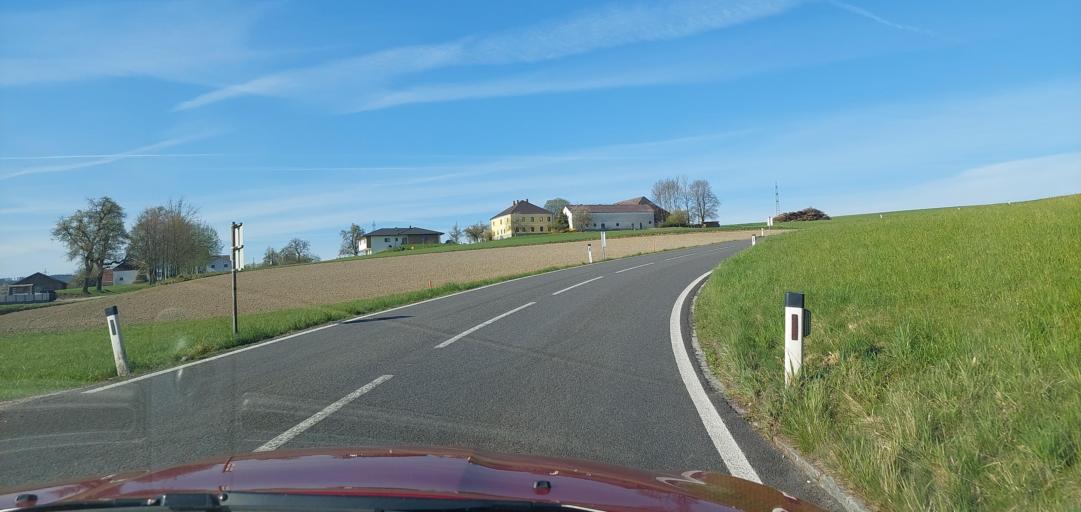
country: AT
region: Upper Austria
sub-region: Politischer Bezirk Ried im Innkreis
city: Ried im Innkreis
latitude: 48.1761
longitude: 13.5424
